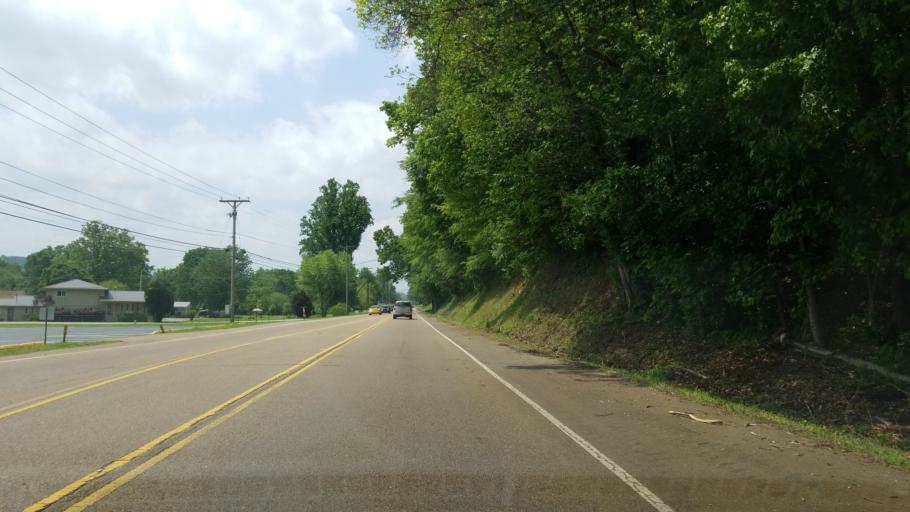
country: US
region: Tennessee
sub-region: Hamilton County
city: Falling Water
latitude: 35.2152
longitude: -85.2282
